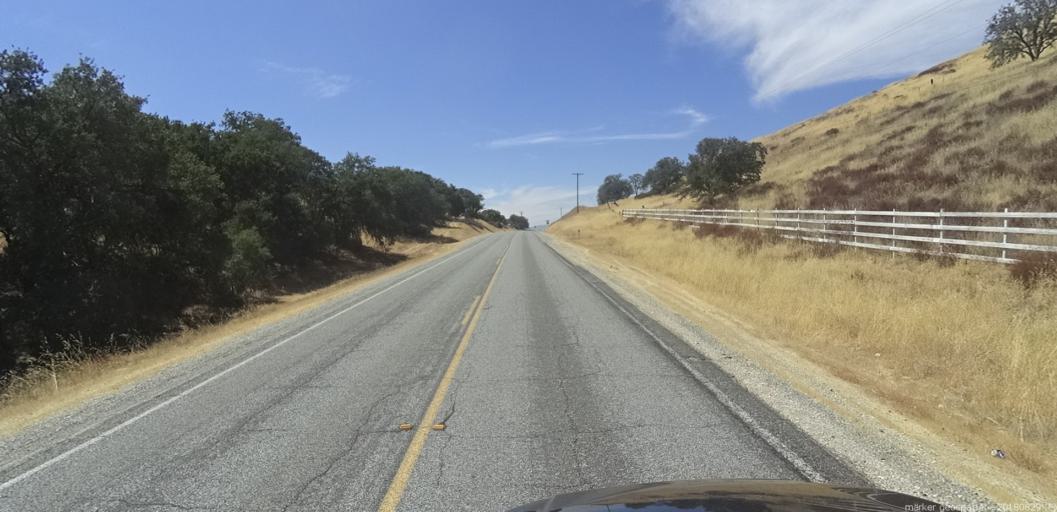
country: US
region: California
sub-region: San Luis Obispo County
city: Lake Nacimiento
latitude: 35.9081
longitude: -121.0101
